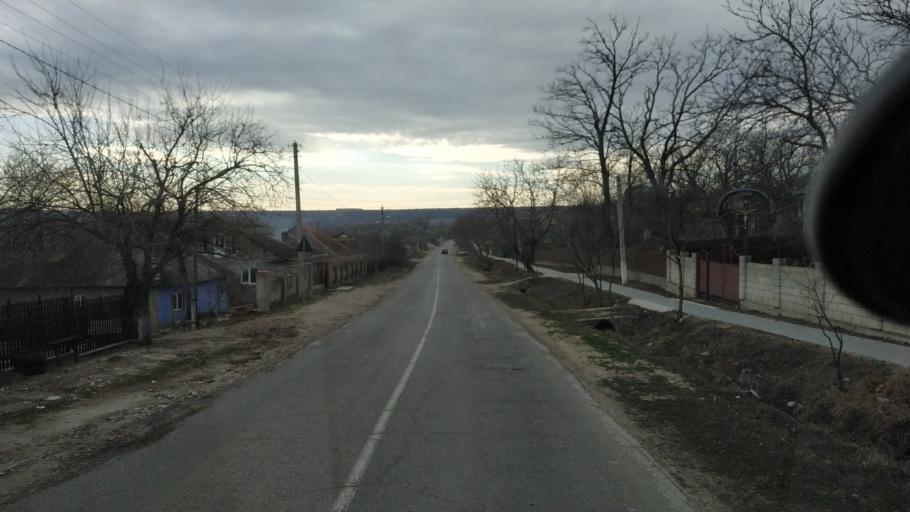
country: MD
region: Chisinau
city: Vadul lui Voda
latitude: 47.1478
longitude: 29.0794
